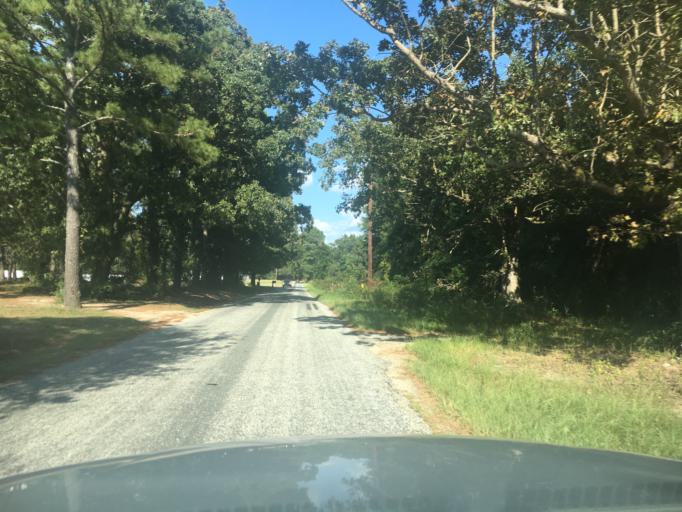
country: US
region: South Carolina
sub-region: Greenwood County
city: Ware Shoals
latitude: 34.4640
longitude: -82.2478
